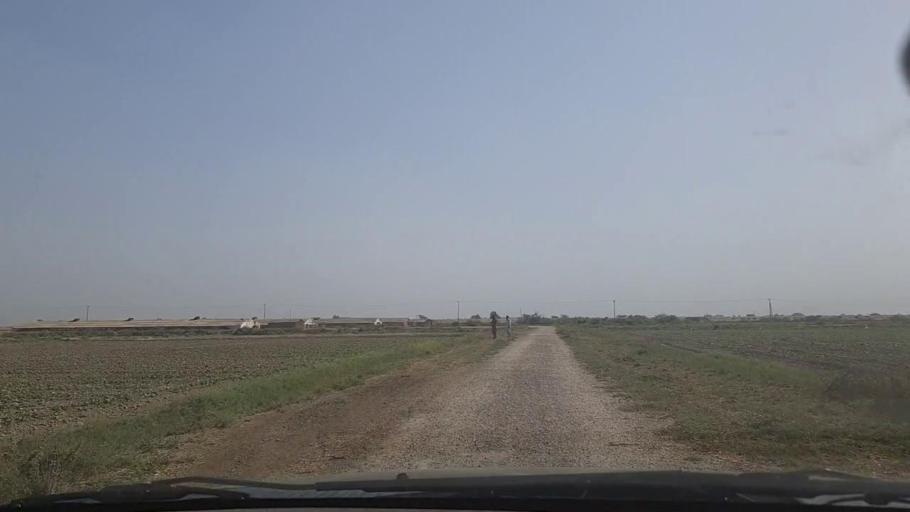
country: PK
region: Sindh
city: Keti Bandar
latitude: 24.1991
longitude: 67.5493
